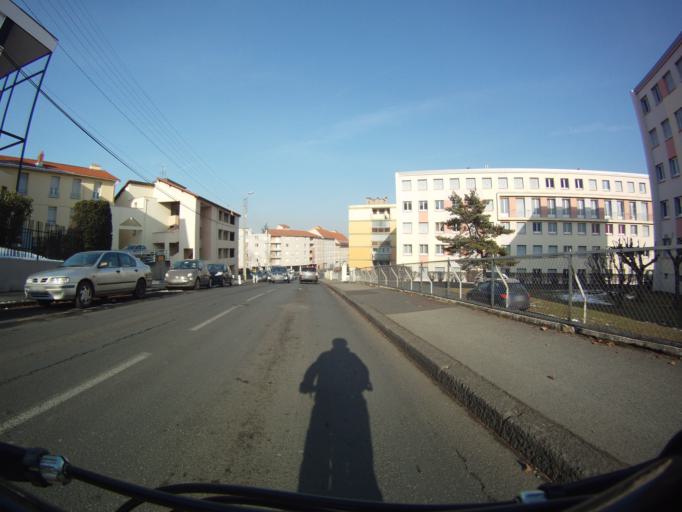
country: FR
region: Auvergne
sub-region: Departement du Puy-de-Dome
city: Aubiere
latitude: 45.7649
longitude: 3.1048
